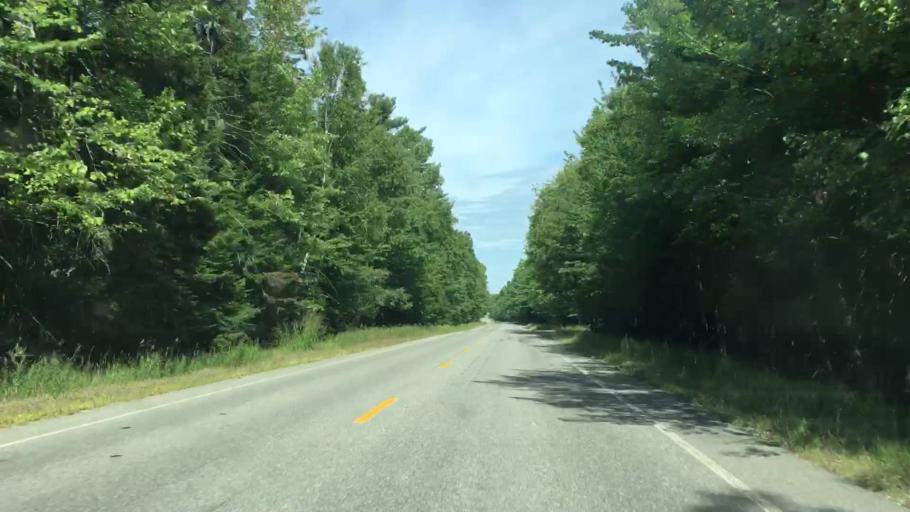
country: US
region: Maine
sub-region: Penobscot County
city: Lincoln
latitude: 45.3813
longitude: -68.5458
